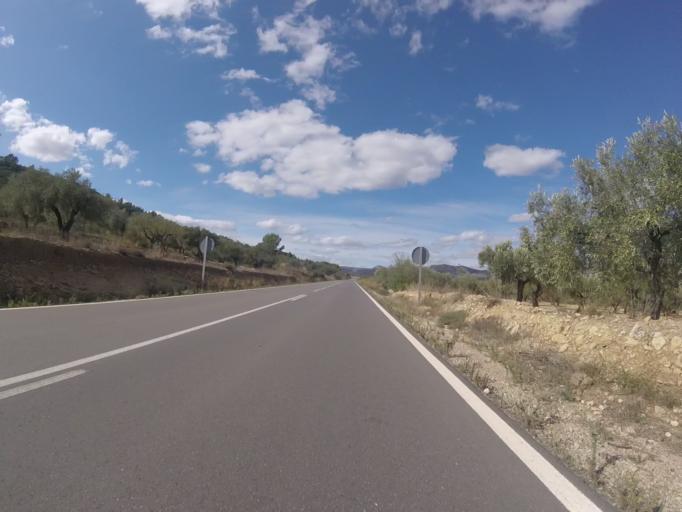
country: ES
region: Valencia
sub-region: Provincia de Castello
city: Chert/Xert
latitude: 40.4369
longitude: 0.1286
